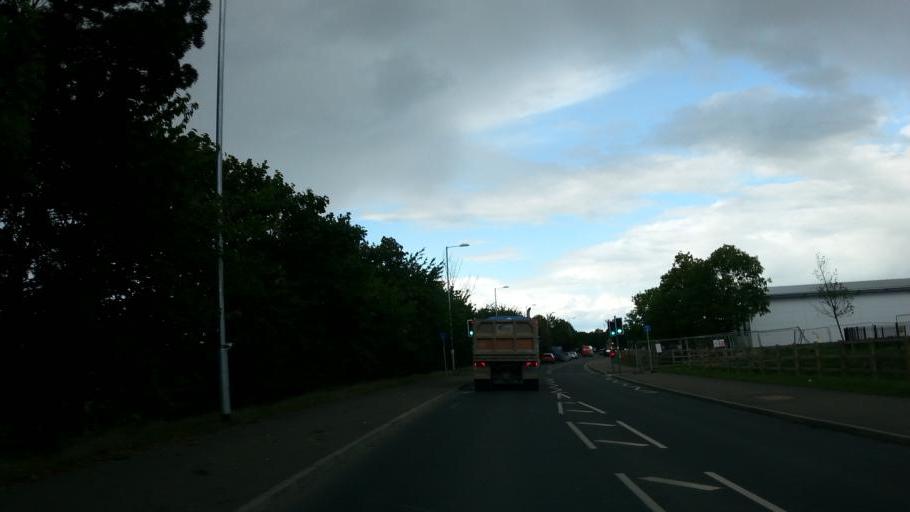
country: GB
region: England
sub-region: Cambridgeshire
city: Godmanchester
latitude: 52.3114
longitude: -0.1641
